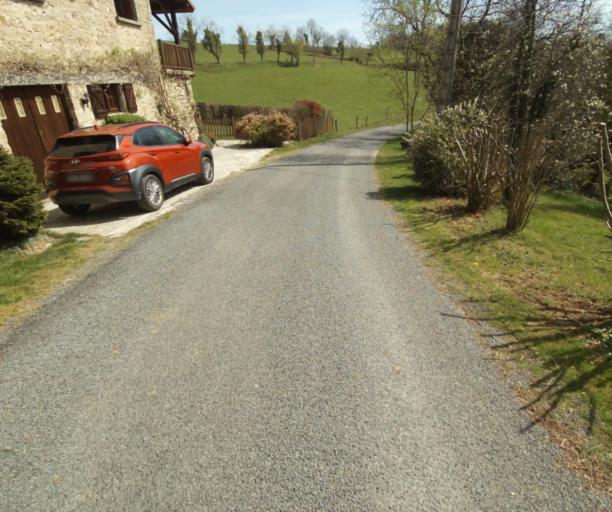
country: FR
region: Limousin
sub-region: Departement de la Correze
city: Naves
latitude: 45.3810
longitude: 1.7994
